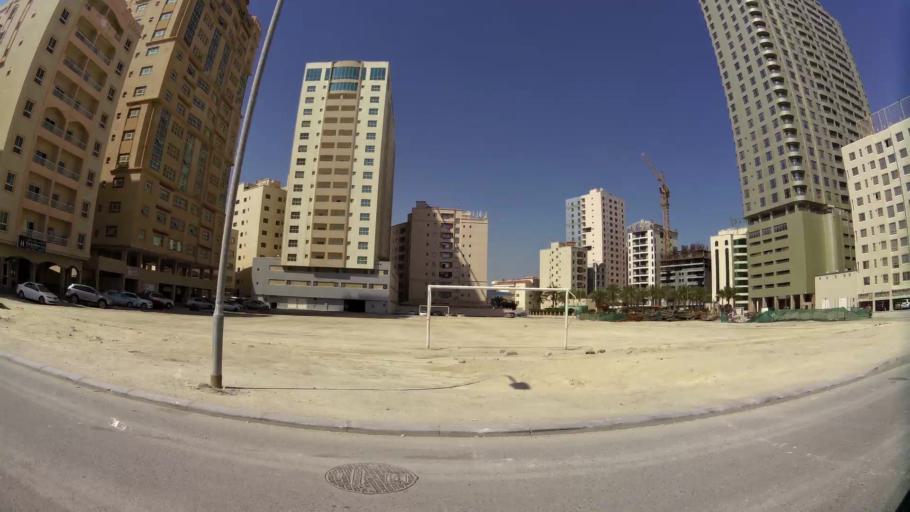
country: BH
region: Manama
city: Manama
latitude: 26.2133
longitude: 50.6003
